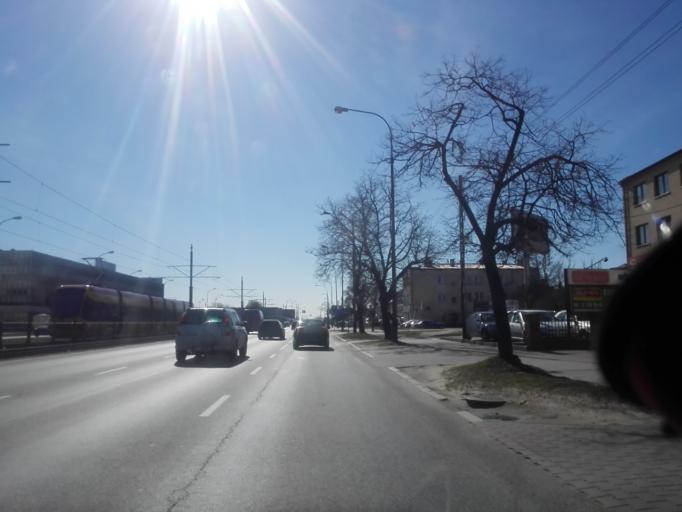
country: PL
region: Masovian Voivodeship
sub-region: Warszawa
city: Wlochy
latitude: 52.1785
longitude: 20.9463
